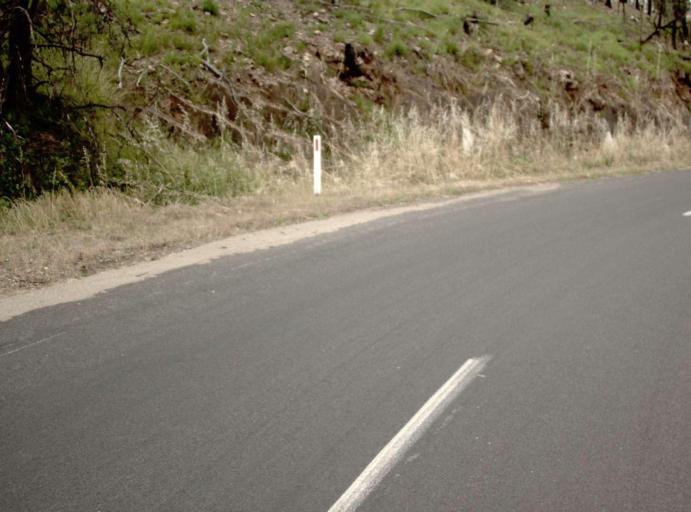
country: AU
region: Victoria
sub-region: Wellington
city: Heyfield
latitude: -37.8484
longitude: 146.7076
